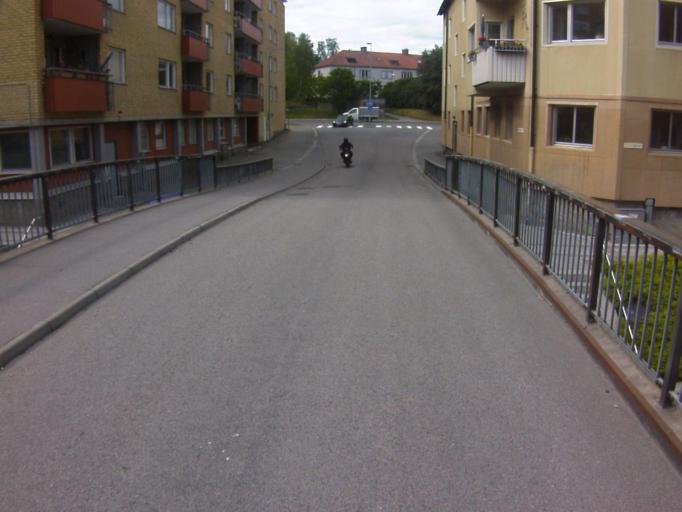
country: SE
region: Soedermanland
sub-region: Eskilstuna Kommun
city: Eskilstuna
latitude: 59.3675
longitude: 16.5066
